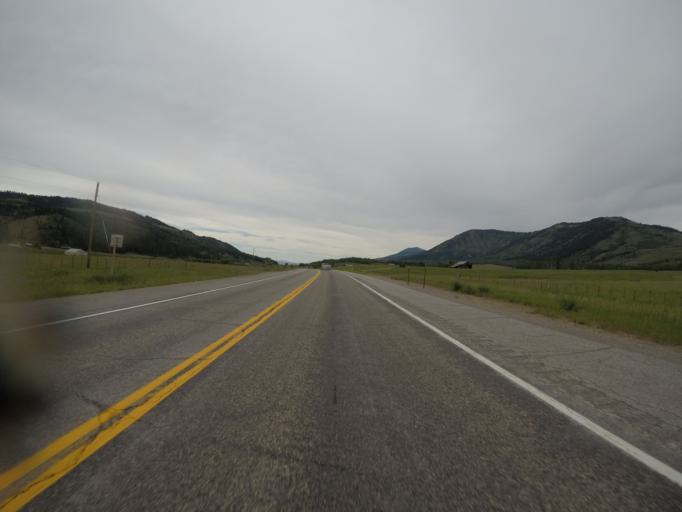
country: US
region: Wyoming
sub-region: Lincoln County
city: Afton
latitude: 42.5570
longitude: -110.8948
